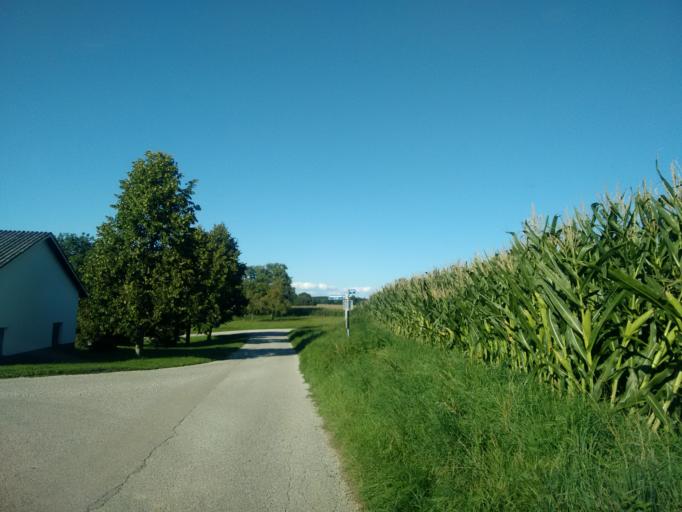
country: AT
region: Upper Austria
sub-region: Politischer Bezirk Kirchdorf an der Krems
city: Kremsmunster
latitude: 48.0827
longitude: 14.1035
